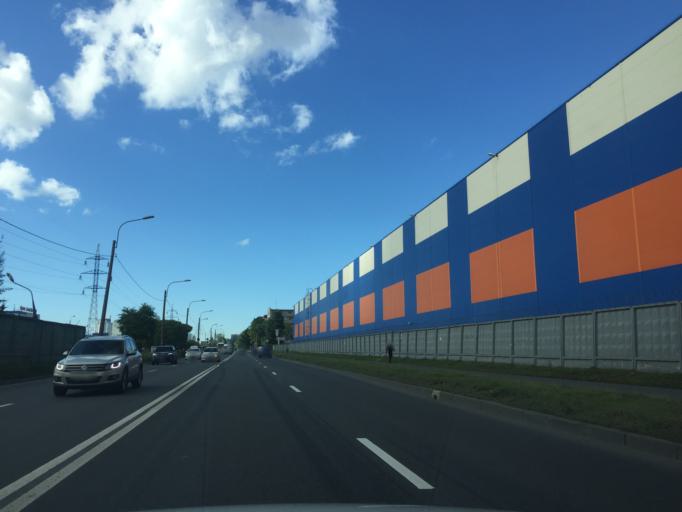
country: RU
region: St.-Petersburg
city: Dachnoye
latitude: 59.8383
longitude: 30.3025
